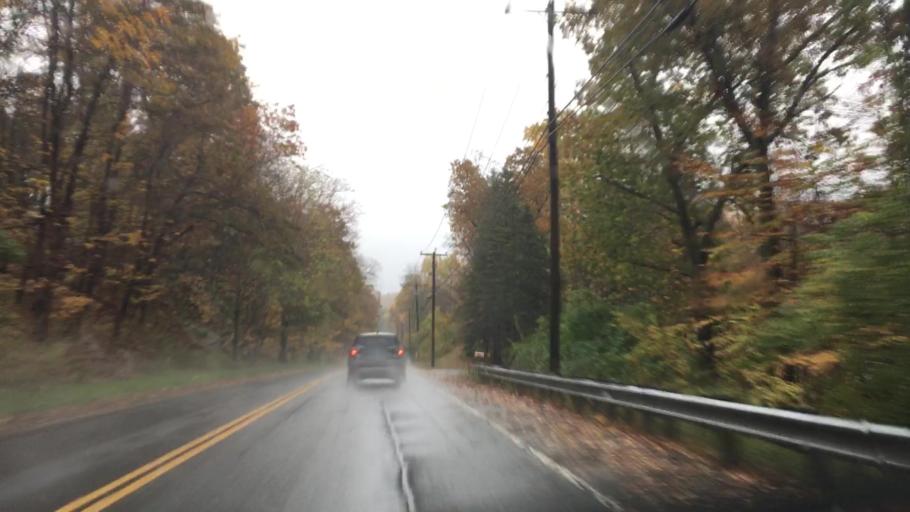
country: US
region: Connecticut
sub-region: Litchfield County
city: New Milford
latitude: 41.5448
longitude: -73.3609
